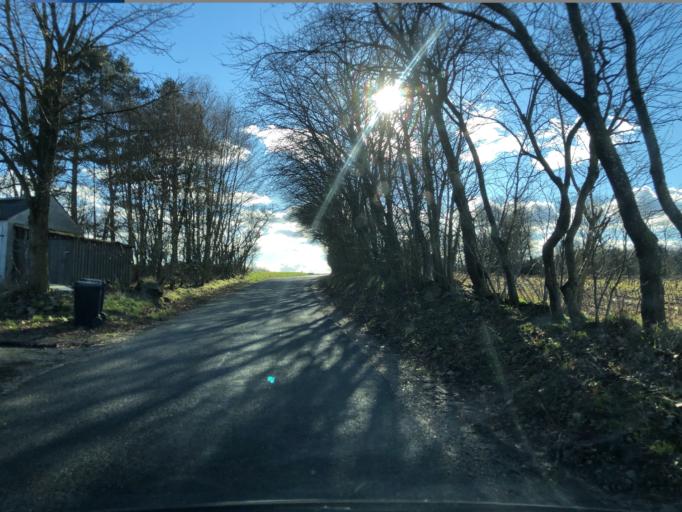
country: DK
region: Central Jutland
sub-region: Silkeborg Kommune
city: Kjellerup
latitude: 56.3443
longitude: 9.5113
